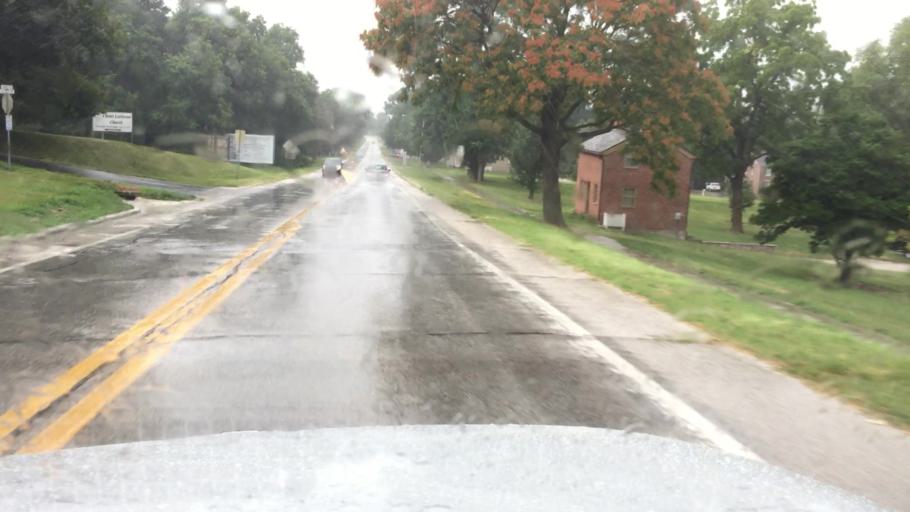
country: US
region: Illinois
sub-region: Hancock County
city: Nauvoo
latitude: 40.5490
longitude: -91.3866
